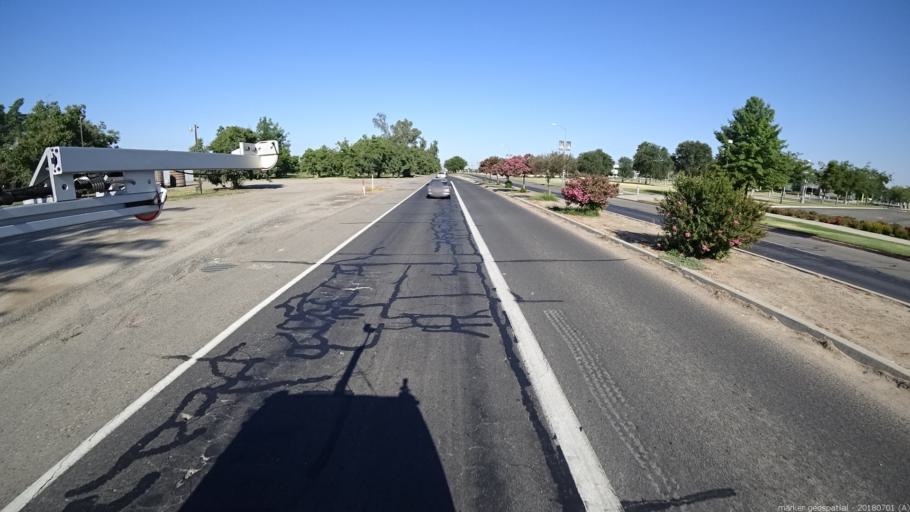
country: US
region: California
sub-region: Madera County
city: Parksdale
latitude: 36.9234
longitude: -119.9962
